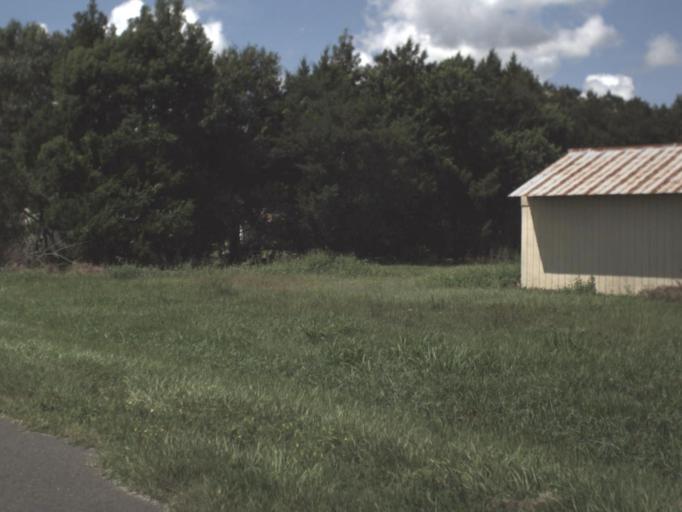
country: US
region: Florida
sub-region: DeSoto County
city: Southeast Arcadia
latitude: 27.1864
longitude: -81.8700
